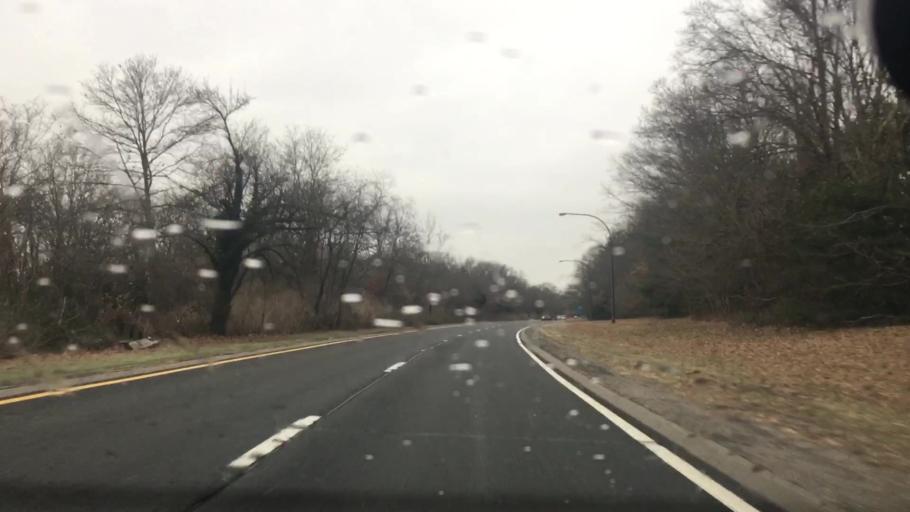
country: US
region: New York
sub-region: Suffolk County
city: South Huntington
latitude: 40.8027
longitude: -73.3863
